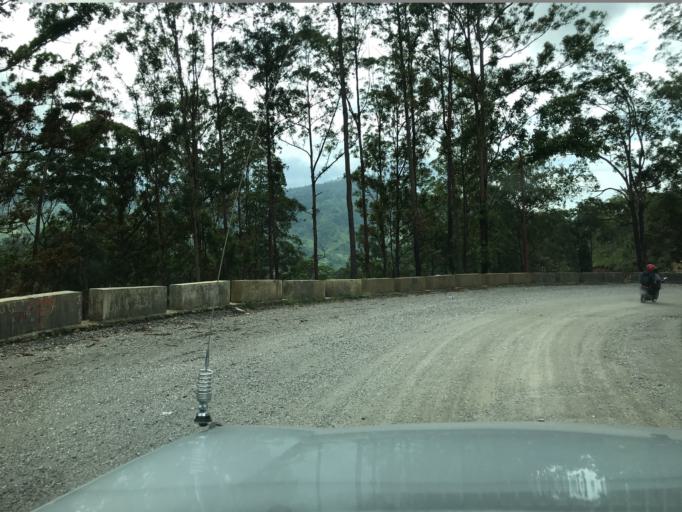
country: TL
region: Aileu
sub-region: Aileu Villa
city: Aileu
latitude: -8.6638
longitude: 125.5351
